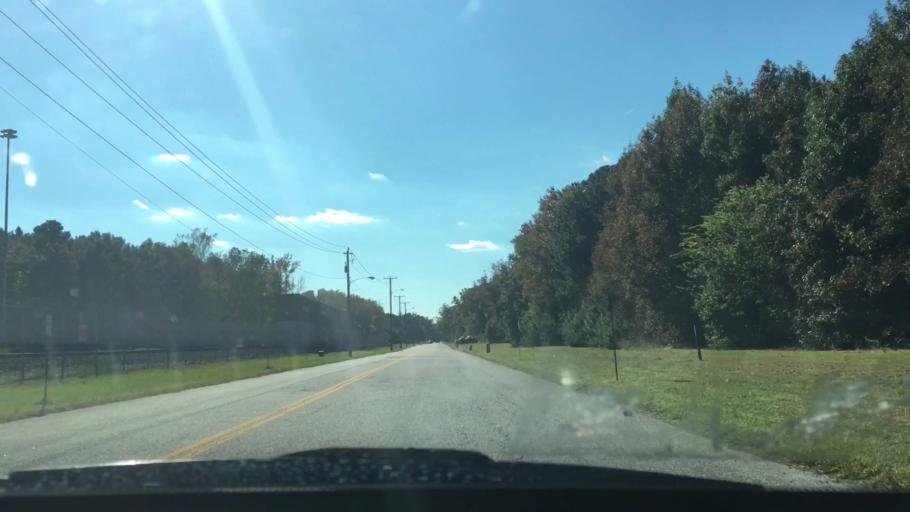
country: US
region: Virginia
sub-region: City of Portsmouth
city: Portsmouth Heights
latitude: 36.8786
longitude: -76.3642
